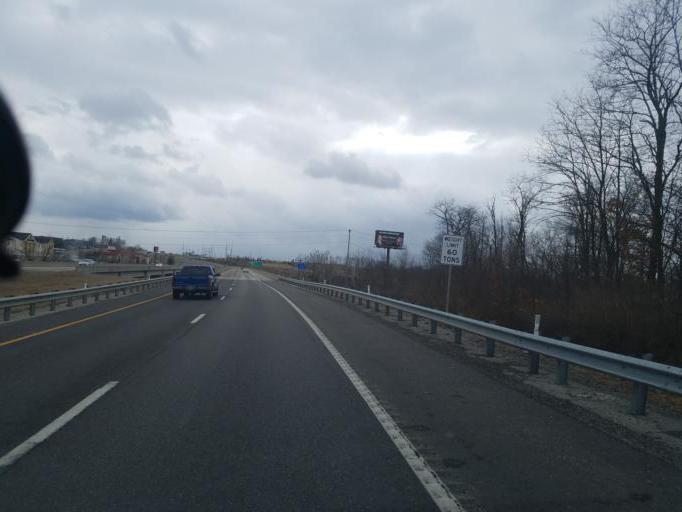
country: US
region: Missouri
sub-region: Boone County
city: Columbia
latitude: 38.9651
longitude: -92.2948
